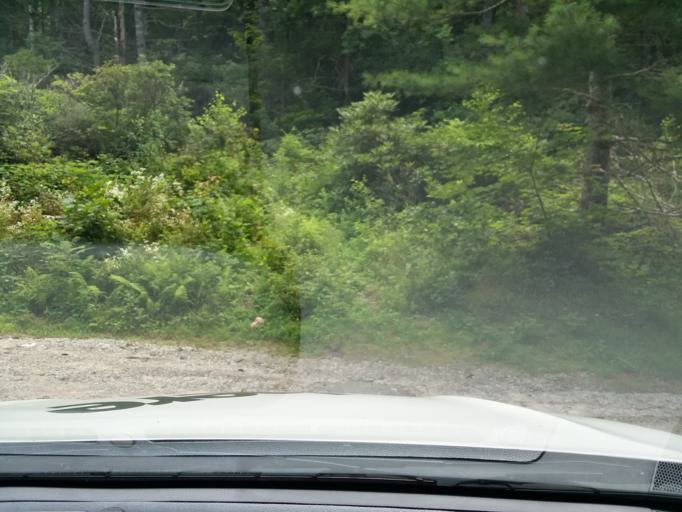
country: US
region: Georgia
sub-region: Rabun County
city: Mountain City
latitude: 35.0333
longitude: -83.2356
